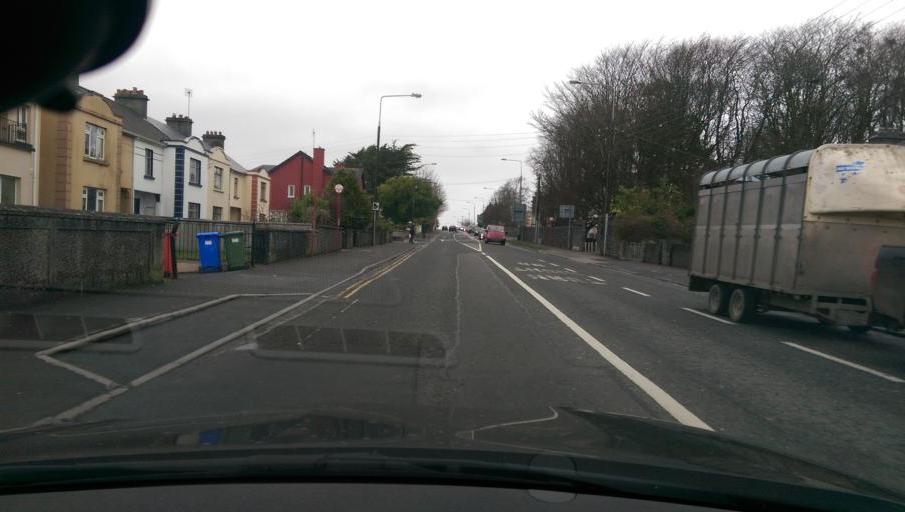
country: IE
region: Connaught
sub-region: County Galway
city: Gaillimh
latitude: 53.2825
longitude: -9.0659
